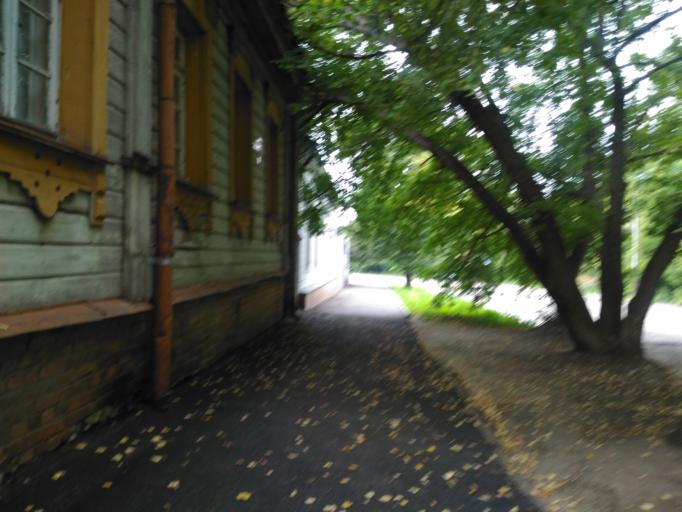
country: RU
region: Ulyanovsk
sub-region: Ulyanovskiy Rayon
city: Ulyanovsk
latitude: 54.3139
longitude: 48.3847
